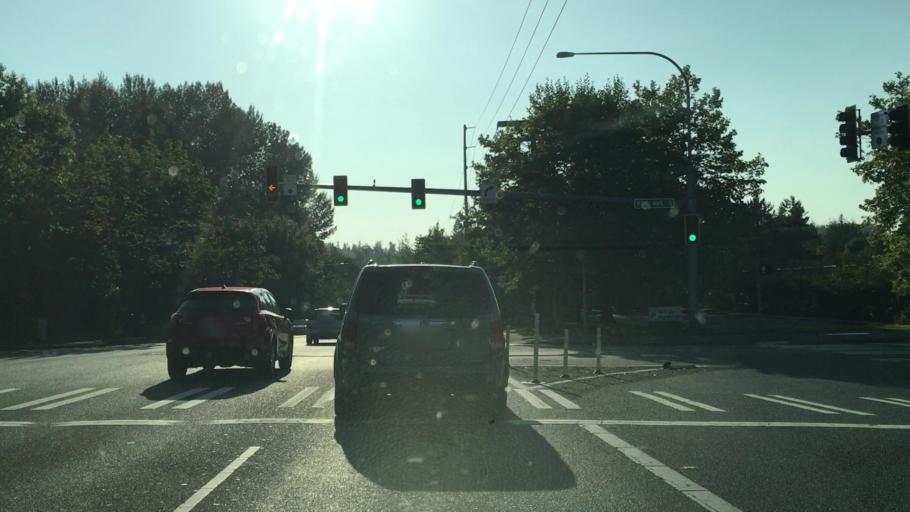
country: US
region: Washington
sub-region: King County
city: Federal Way
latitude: 47.2899
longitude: -122.3227
